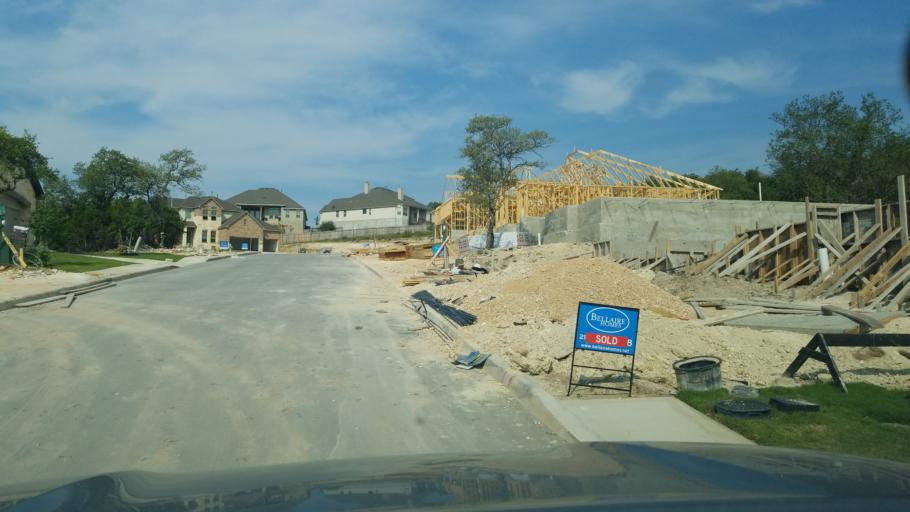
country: US
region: Texas
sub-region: Bexar County
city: Scenic Oaks
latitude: 29.7184
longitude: -98.6541
